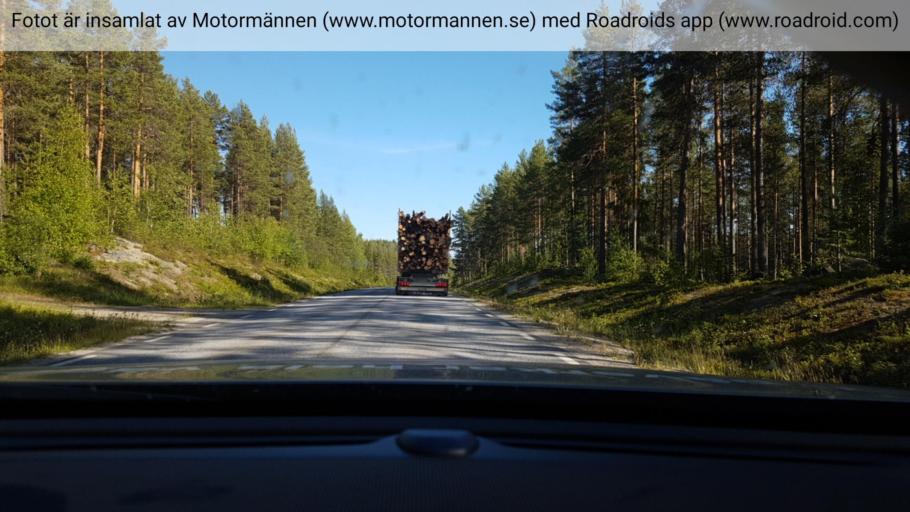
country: SE
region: Vaesterbotten
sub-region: Bjurholms Kommun
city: Bjurholm
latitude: 64.2684
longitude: 19.2693
